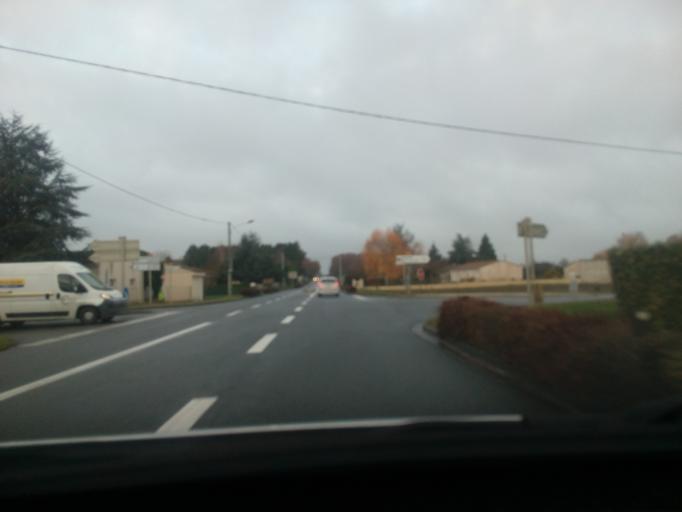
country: FR
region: Poitou-Charentes
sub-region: Departement de la Charente
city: Barbezieux-Saint-Hilaire
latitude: 45.4625
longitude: -0.2032
